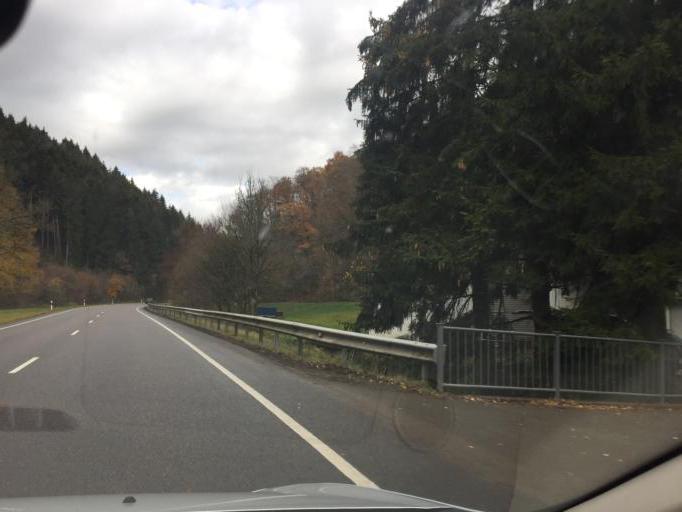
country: LU
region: Diekirch
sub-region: Canton de Wiltz
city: Esch-sur-Sure
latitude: 49.9125
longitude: 5.9493
